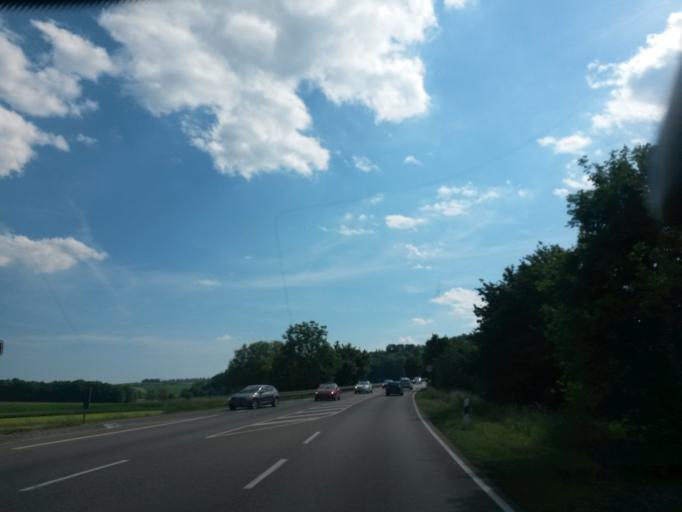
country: DE
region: Baden-Wuerttemberg
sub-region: Regierungsbezirk Stuttgart
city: Renningen
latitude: 48.7609
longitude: 8.9470
